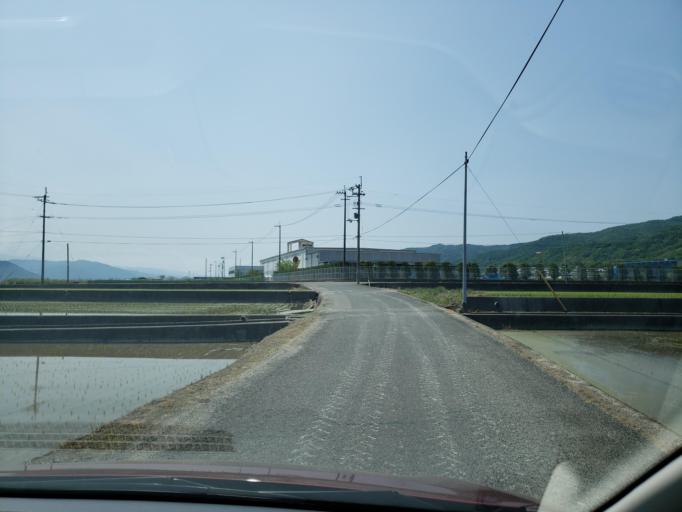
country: JP
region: Tokushima
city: Kamojimacho-jogejima
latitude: 34.0993
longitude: 134.2666
